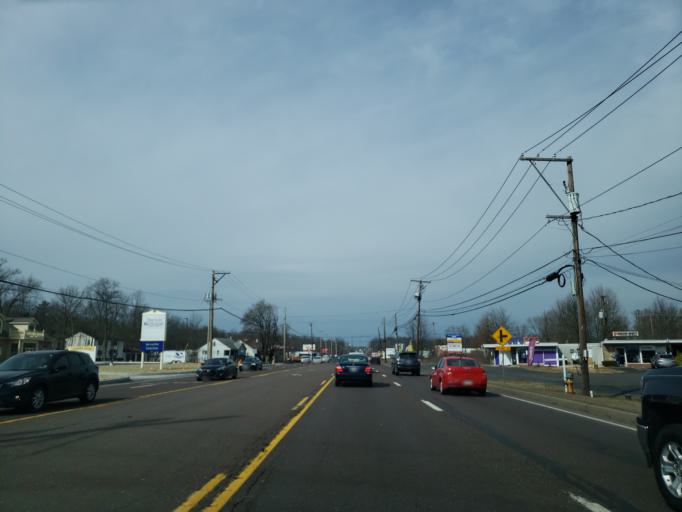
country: US
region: Pennsylvania
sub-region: Bucks County
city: Quakertown
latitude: 40.4504
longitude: -75.3625
